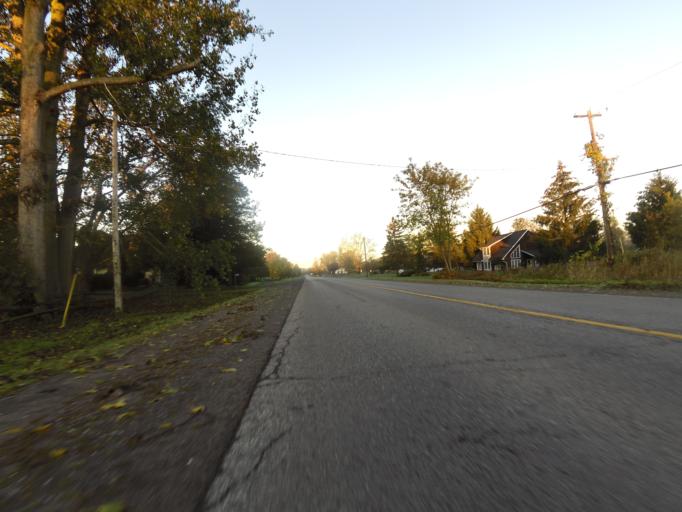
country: CA
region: Ontario
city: Quinte West
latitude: 44.0393
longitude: -77.6394
